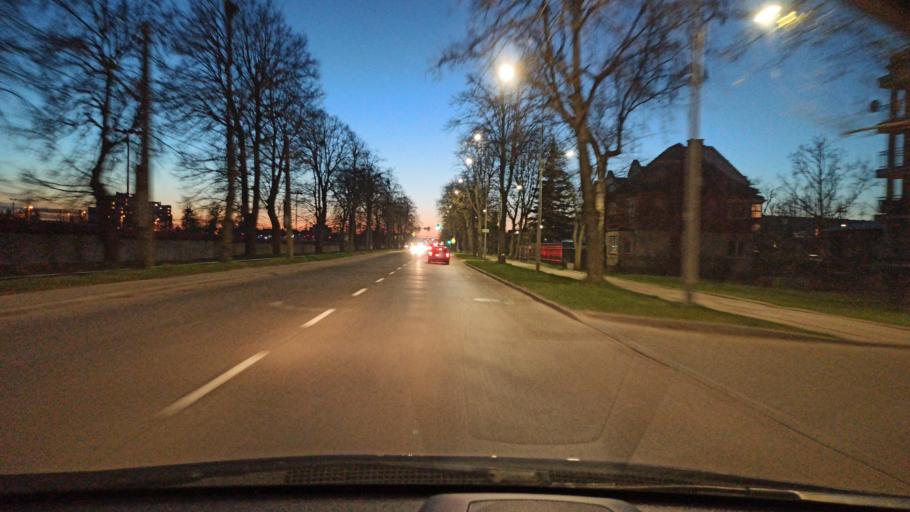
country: PL
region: Warmian-Masurian Voivodeship
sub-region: Powiat elblaski
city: Elblag
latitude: 54.1488
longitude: 19.4284
